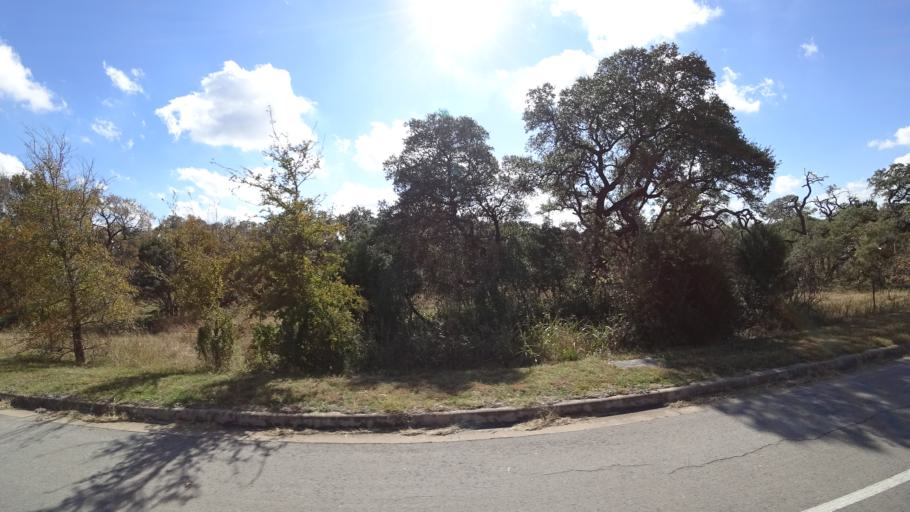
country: US
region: Texas
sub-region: Williamson County
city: Jollyville
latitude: 30.4453
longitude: -97.7378
